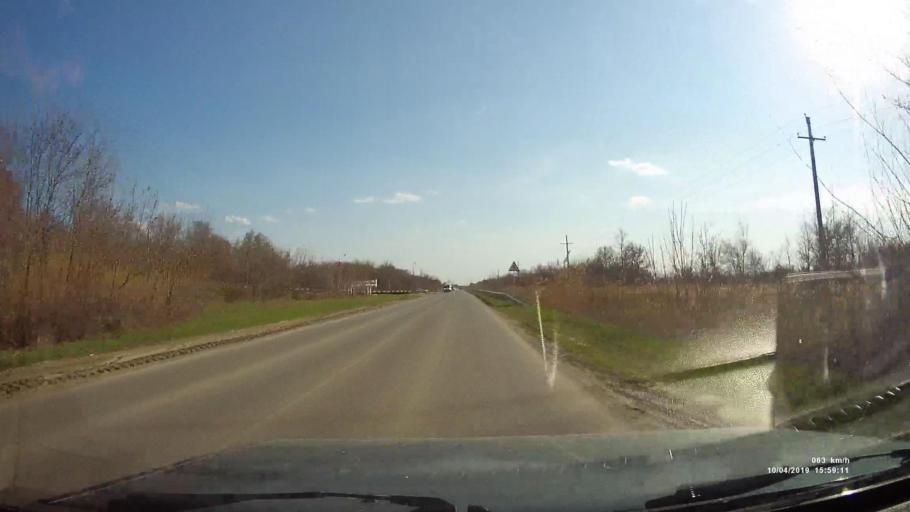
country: RU
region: Rostov
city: Masalovka
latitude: 48.3966
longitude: 40.2694
